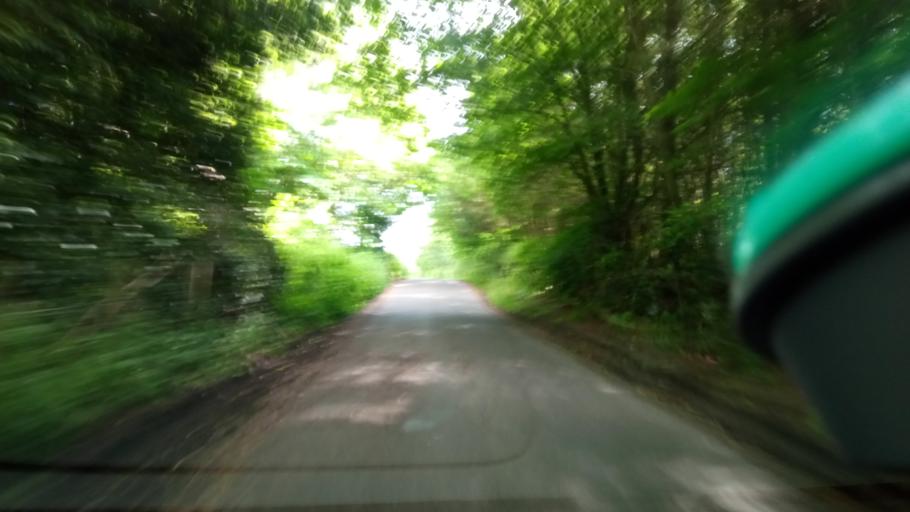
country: GB
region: Scotland
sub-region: The Scottish Borders
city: Jedburgh
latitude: 55.4606
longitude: -2.5474
